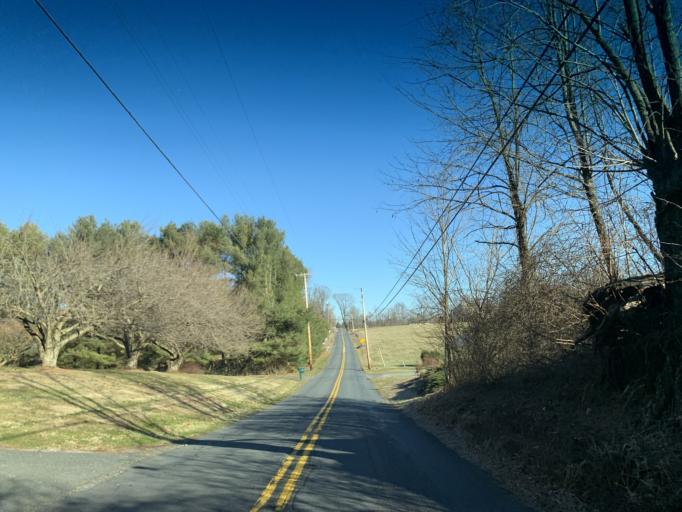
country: US
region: Maryland
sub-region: Harford County
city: Aberdeen
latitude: 39.5913
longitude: -76.2232
